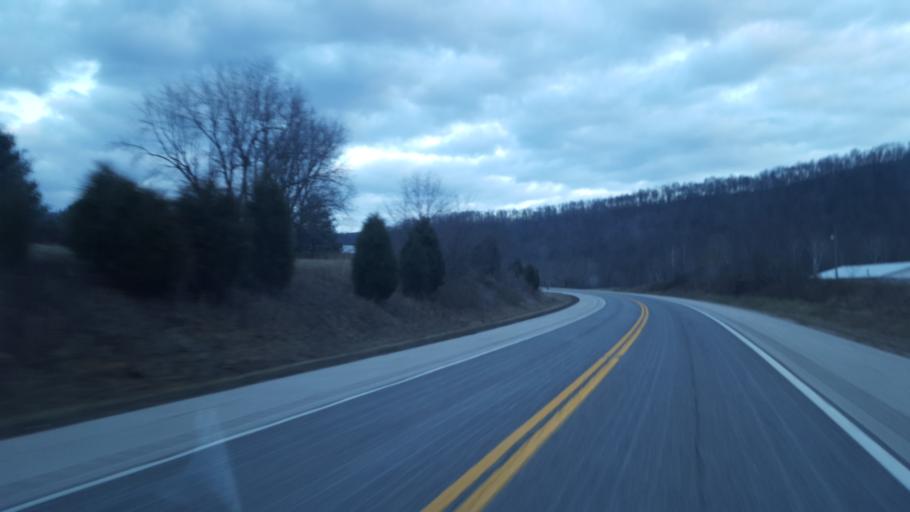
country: US
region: Kentucky
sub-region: Lewis County
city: Vanceburg
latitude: 38.5830
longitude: -83.3651
